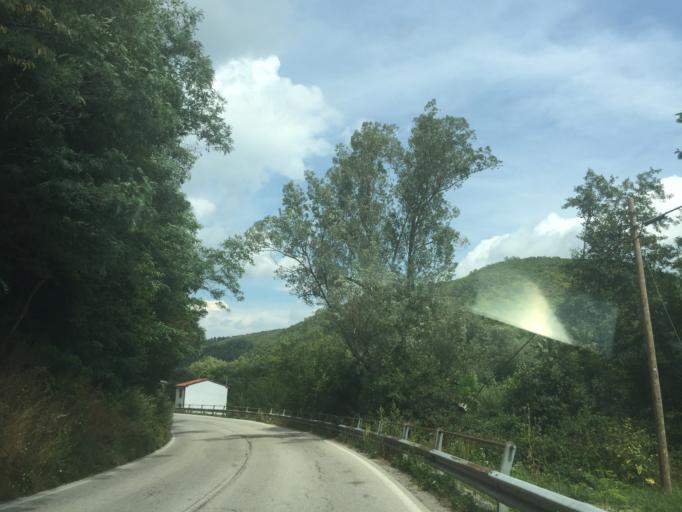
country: IT
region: Tuscany
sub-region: Provincia di Pistoia
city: Campo Tizzoro
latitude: 44.0119
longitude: 10.8563
